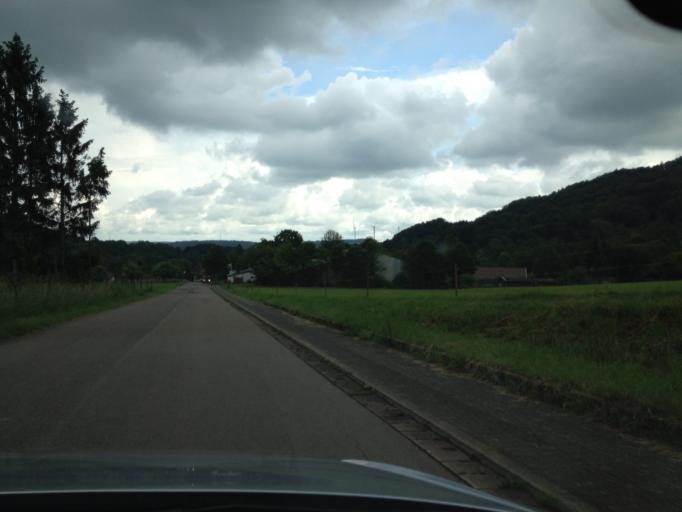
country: DE
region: Saarland
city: Freisen
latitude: 49.5358
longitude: 7.2602
